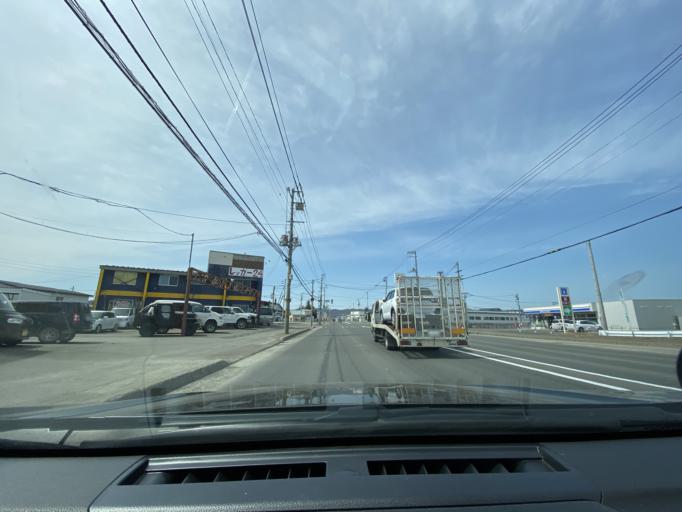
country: JP
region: Hokkaido
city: Kitami
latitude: 43.7971
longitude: 143.8370
